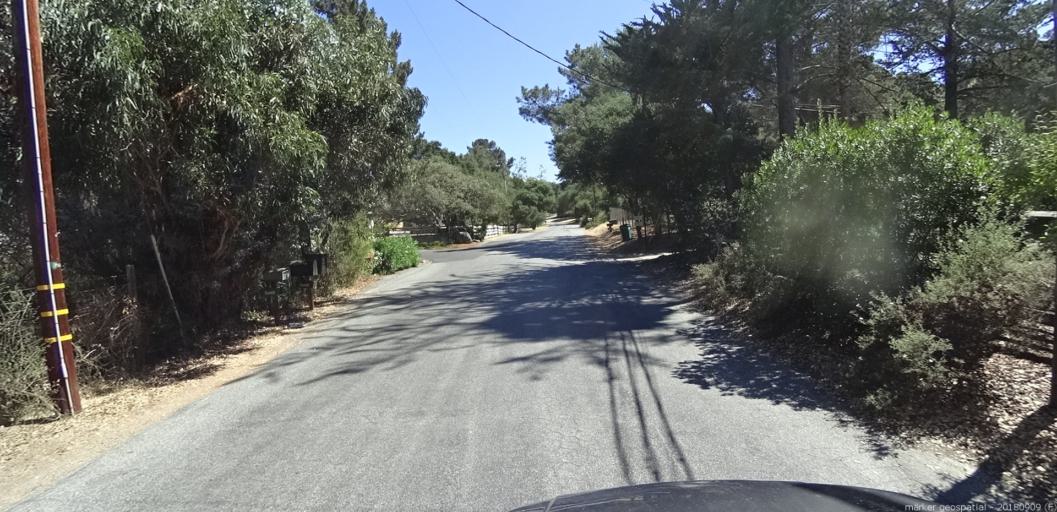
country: US
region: California
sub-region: Monterey County
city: Carmel Valley Village
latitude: 36.5677
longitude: -121.7026
